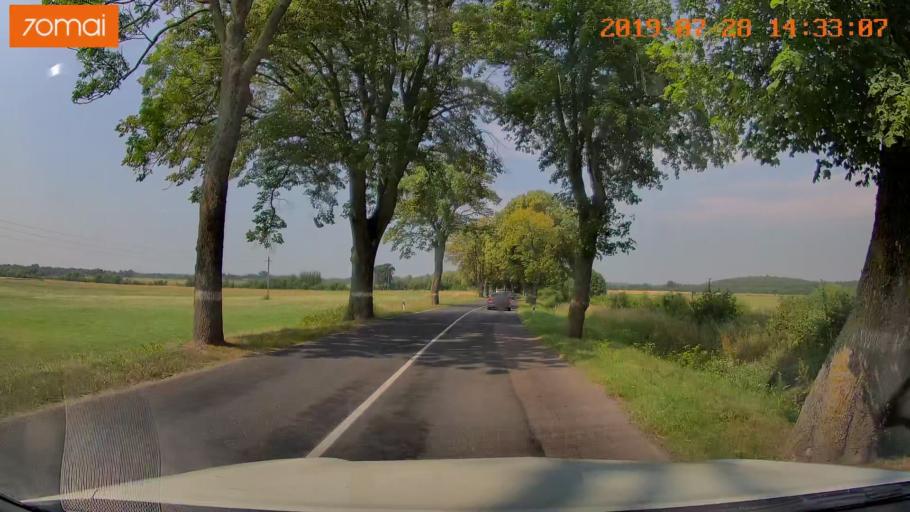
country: RU
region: Kaliningrad
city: Primorsk
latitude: 54.8173
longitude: 20.0348
